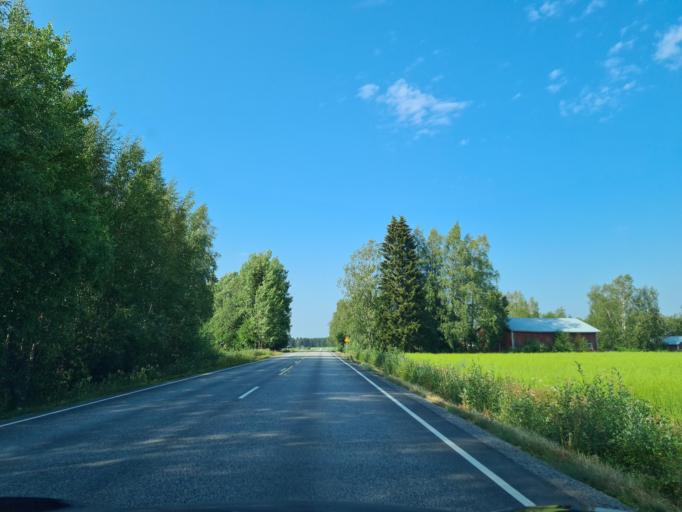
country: FI
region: Satakunta
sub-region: Pohjois-Satakunta
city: Kankaanpaeae
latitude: 61.9044
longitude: 22.4987
